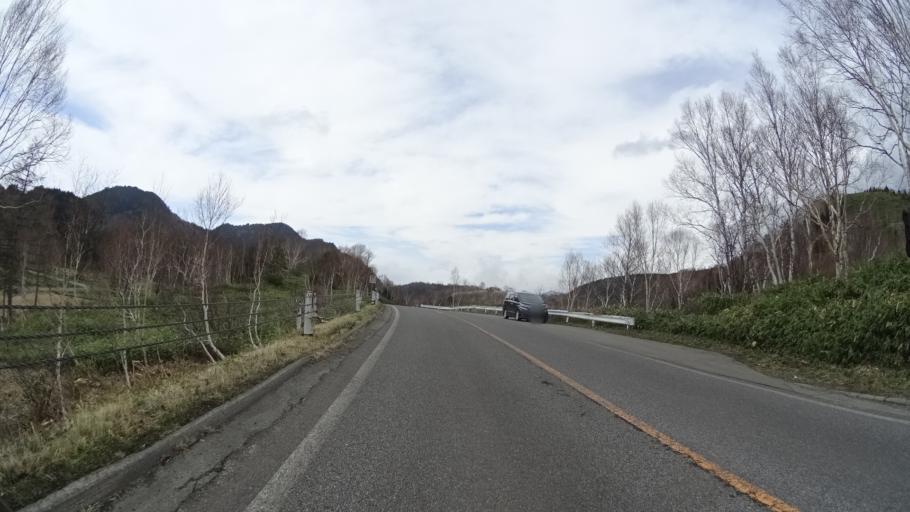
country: JP
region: Nagano
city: Nakano
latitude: 36.6936
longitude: 138.4917
